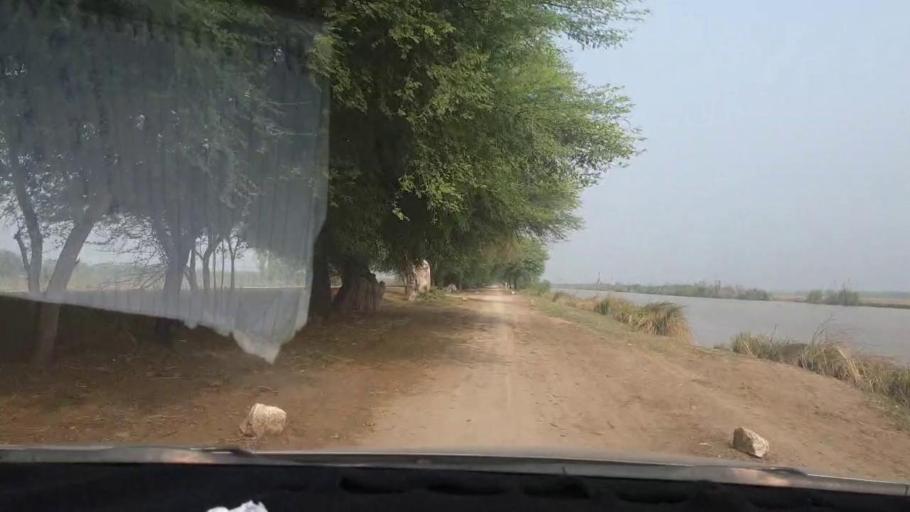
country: PK
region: Sindh
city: Tando Adam
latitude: 25.6758
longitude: 68.5574
